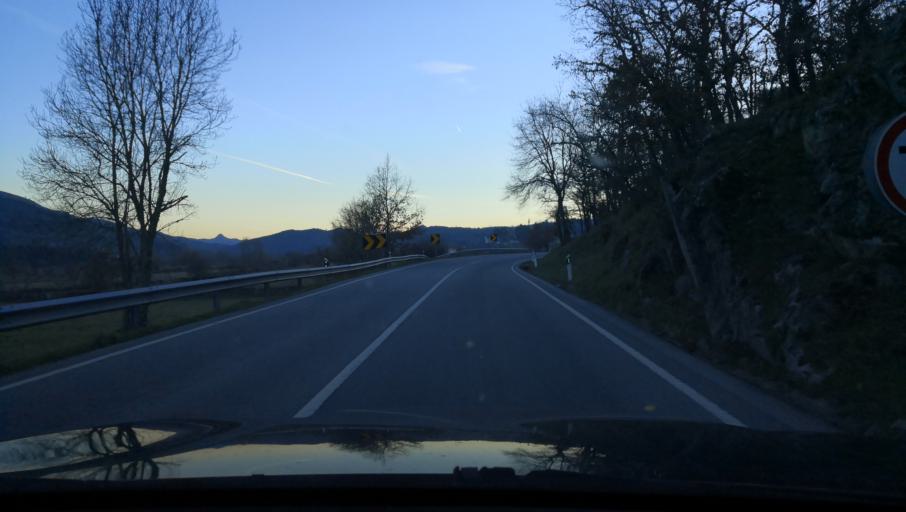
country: PT
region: Vila Real
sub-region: Vila Pouca de Aguiar
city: Vila Pouca de Aguiar
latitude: 41.4288
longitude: -7.6815
